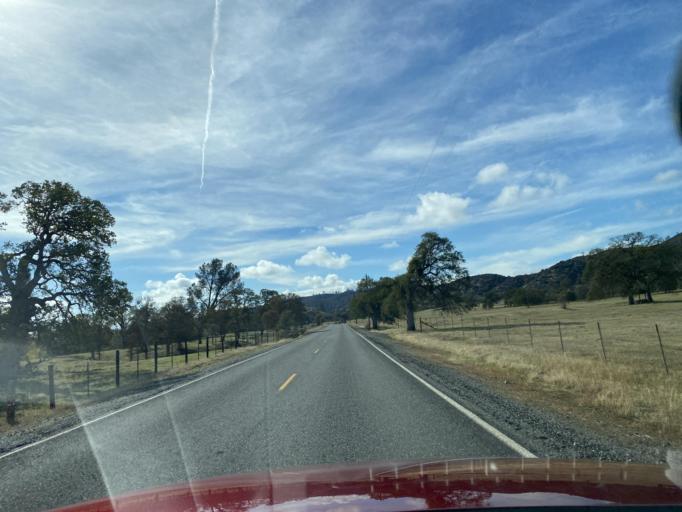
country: US
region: California
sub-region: Glenn County
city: Willows
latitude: 39.4592
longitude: -122.5128
